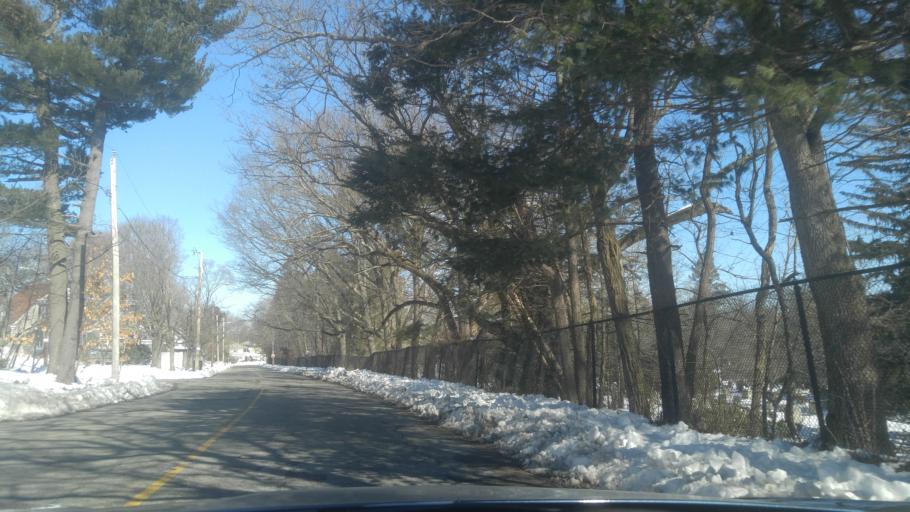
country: US
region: Rhode Island
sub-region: Providence County
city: Pawtucket
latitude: 41.8594
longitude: -71.3837
